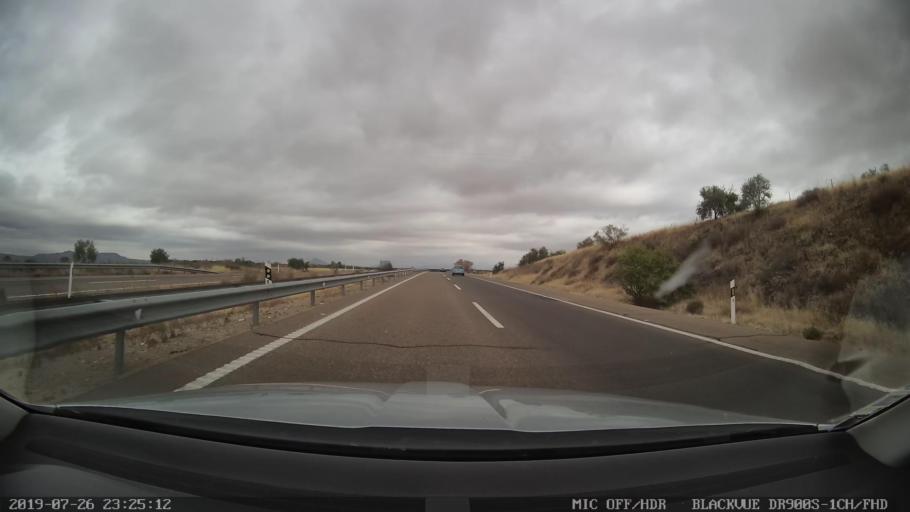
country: ES
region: Extremadura
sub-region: Provincia de Caceres
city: Escurial
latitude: 39.1861
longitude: -5.8944
